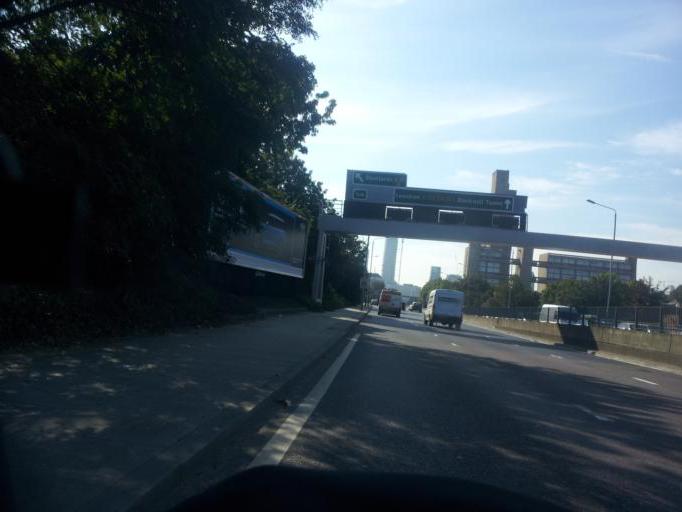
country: GB
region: England
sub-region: Greater London
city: Poplar
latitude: 51.5169
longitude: -0.0091
